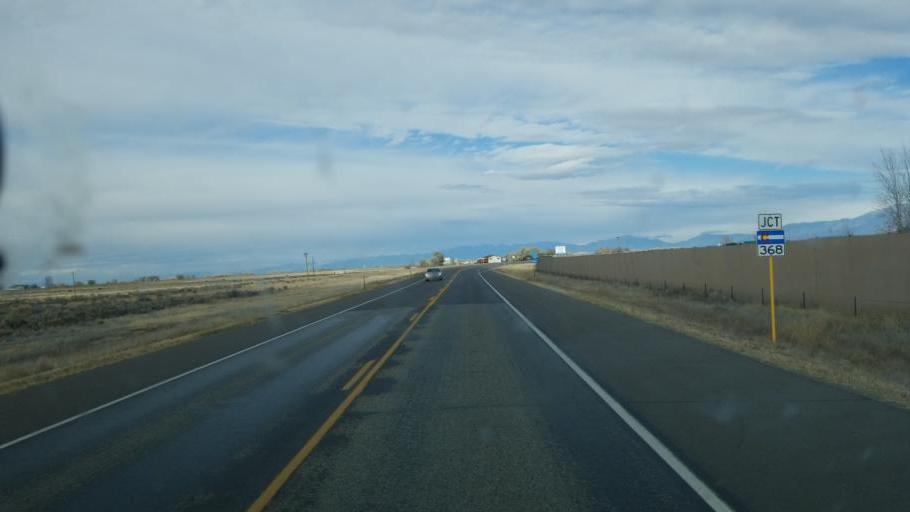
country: US
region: Colorado
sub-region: Alamosa County
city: Alamosa
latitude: 37.3678
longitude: -105.9256
